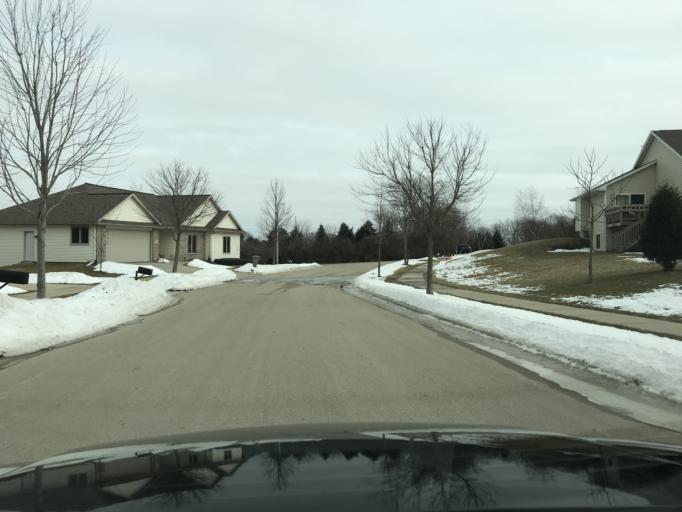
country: US
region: Wisconsin
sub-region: Dane County
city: Monona
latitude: 43.0968
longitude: -89.2711
